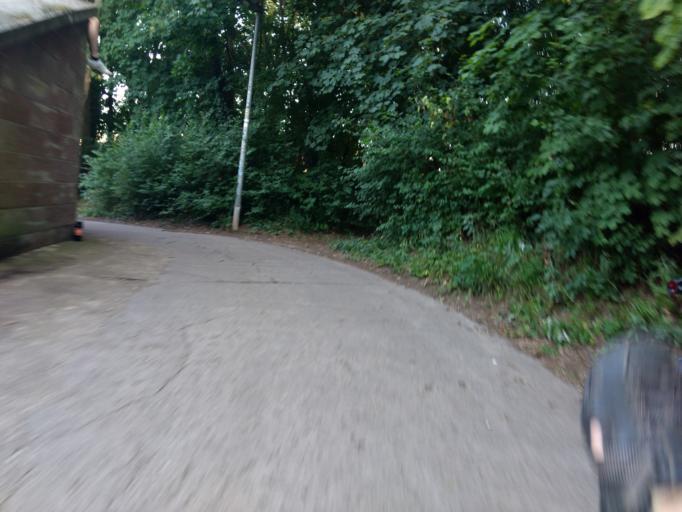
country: DE
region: Saarland
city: Saarlouis
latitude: 49.3156
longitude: 6.7440
